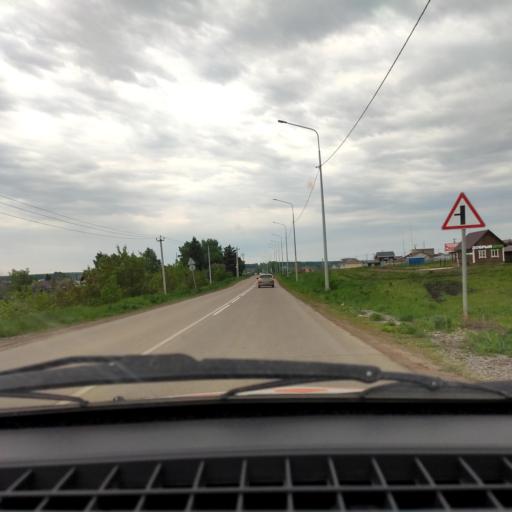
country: RU
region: Bashkortostan
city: Avdon
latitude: 54.5570
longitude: 55.7622
